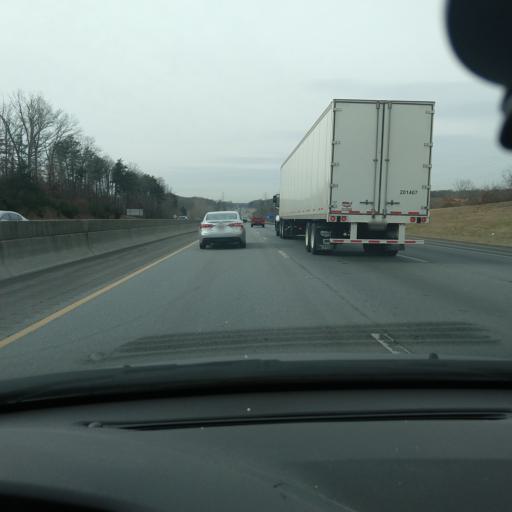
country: US
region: North Carolina
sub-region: Gaston County
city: Bessemer City
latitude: 35.2719
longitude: -81.2429
